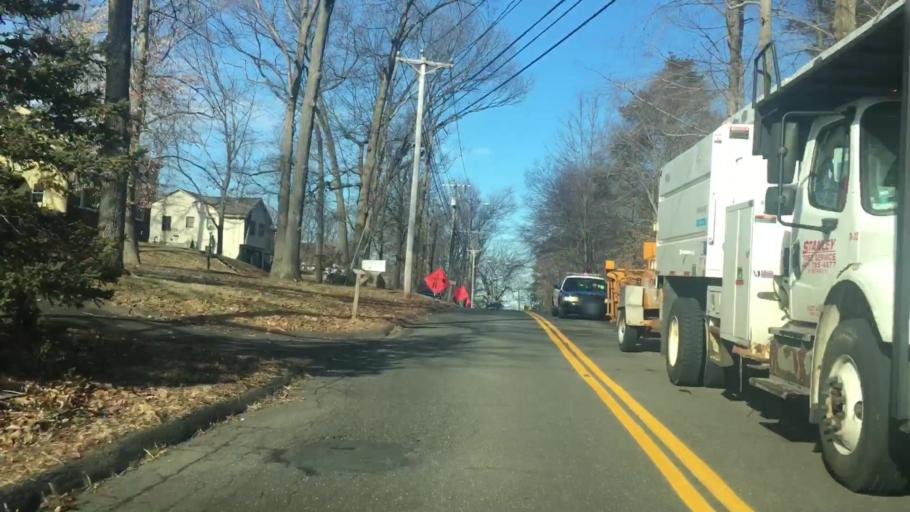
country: US
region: Connecticut
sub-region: Middlesex County
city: Middletown
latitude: 41.5165
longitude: -72.6486
